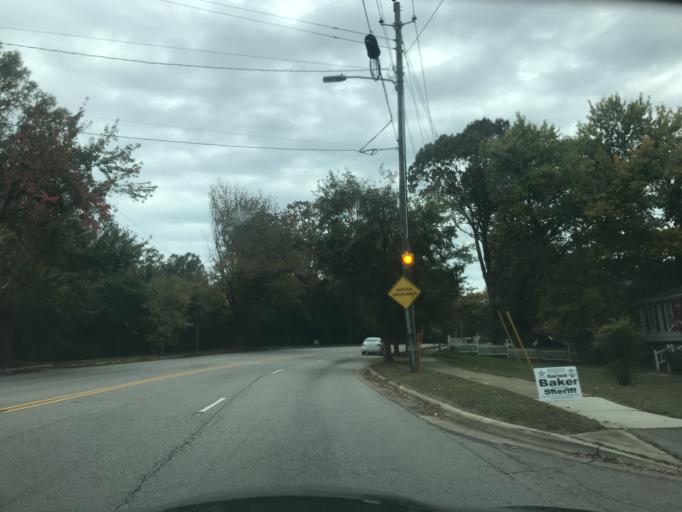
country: US
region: North Carolina
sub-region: Wake County
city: West Raleigh
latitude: 35.8522
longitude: -78.6339
